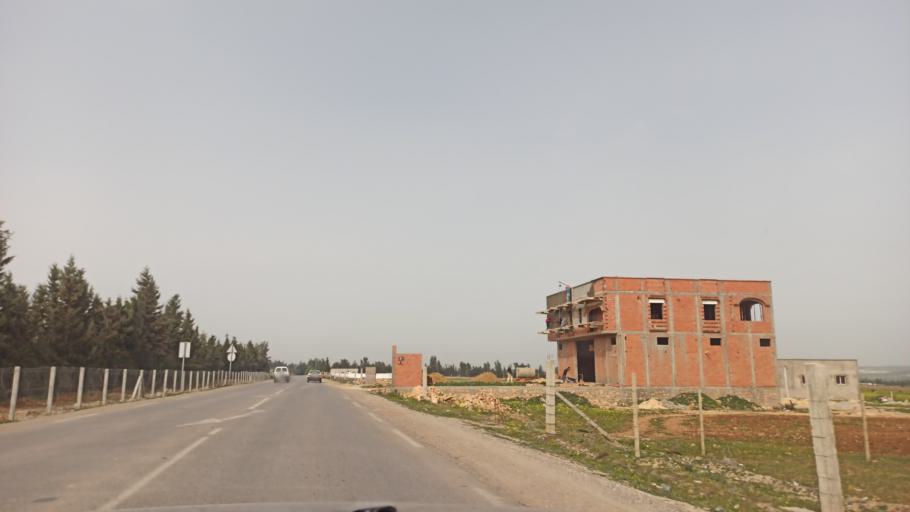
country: TN
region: Zaghwan
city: Zaghouan
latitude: 36.4190
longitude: 10.1035
